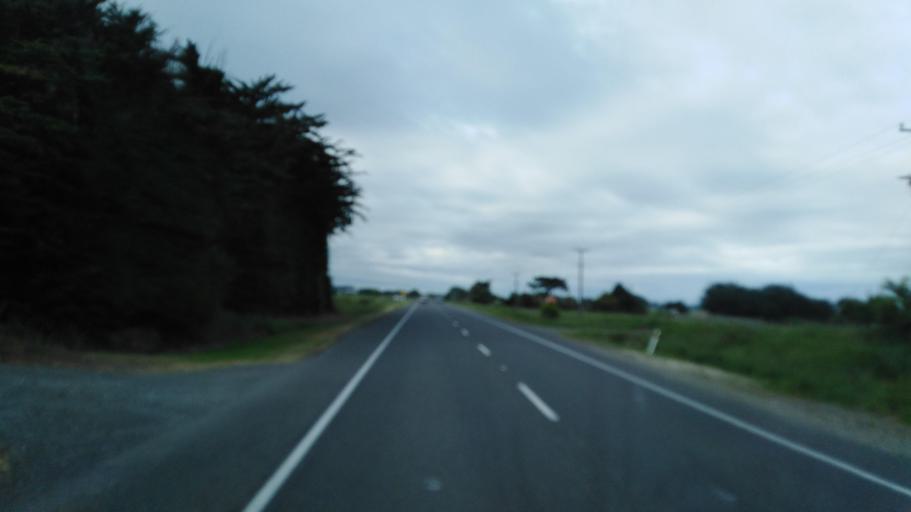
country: NZ
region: Manawatu-Wanganui
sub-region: Rangitikei District
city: Bulls
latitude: -40.2549
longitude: 175.3910
